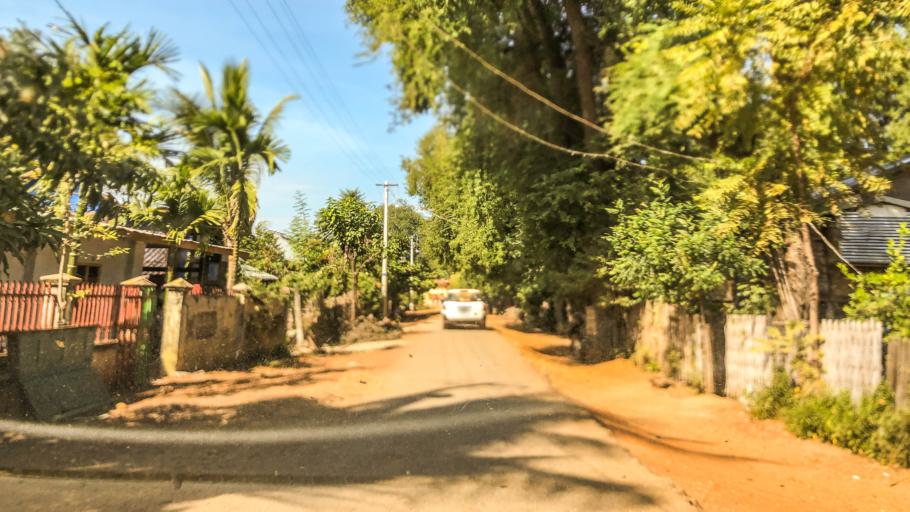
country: MM
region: Magway
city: Magway
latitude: 19.9747
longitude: 95.0380
